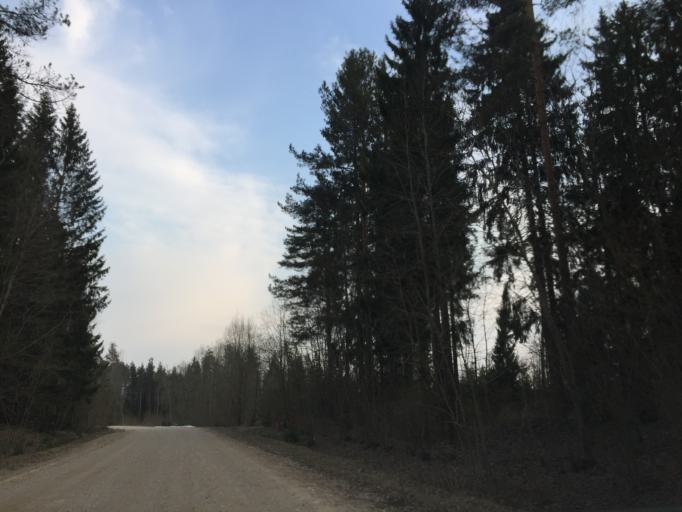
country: LV
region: Raunas
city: Rauna
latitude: 57.1439
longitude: 25.6000
